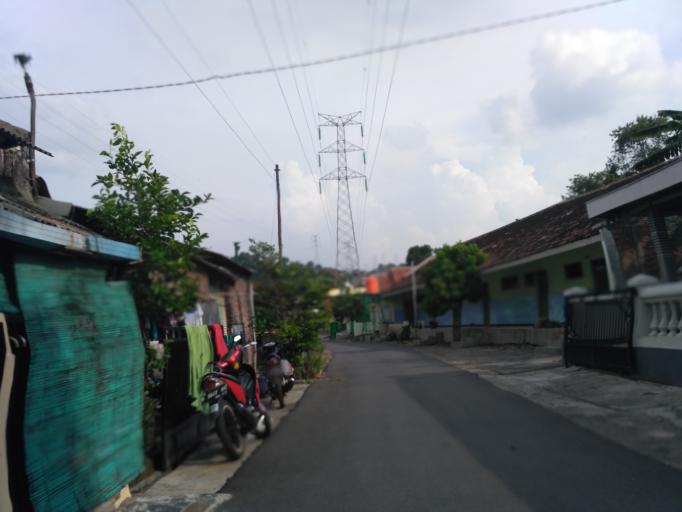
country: ID
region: Central Java
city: Semarang
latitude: -7.0164
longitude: 110.4440
